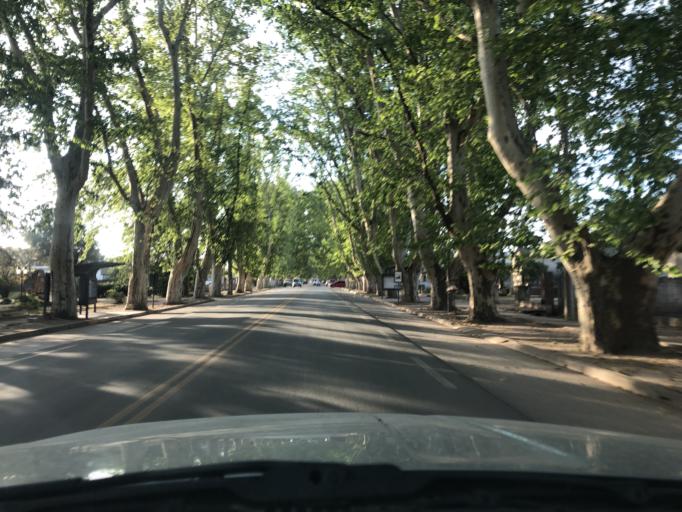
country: AR
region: Cordoba
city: Jesus Maria
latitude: -31.0113
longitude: -64.0734
